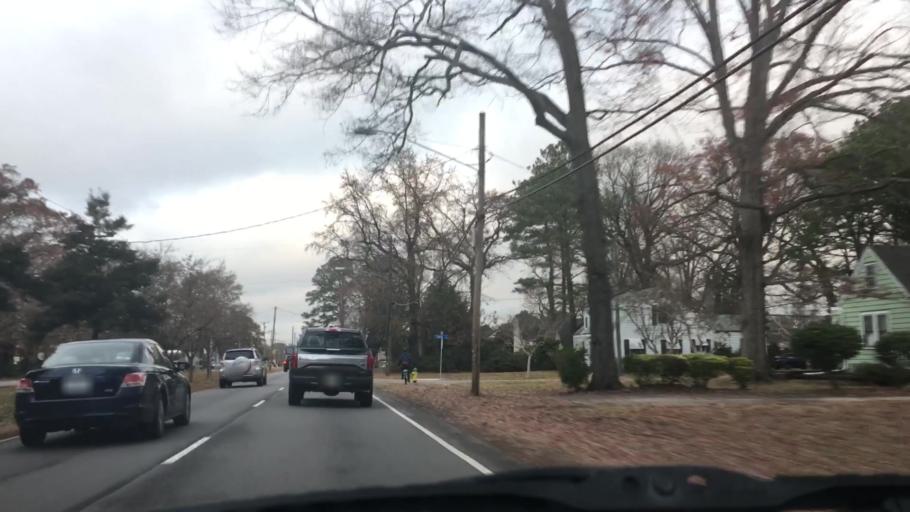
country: US
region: Virginia
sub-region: City of Norfolk
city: Norfolk
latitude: 36.9270
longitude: -76.2433
